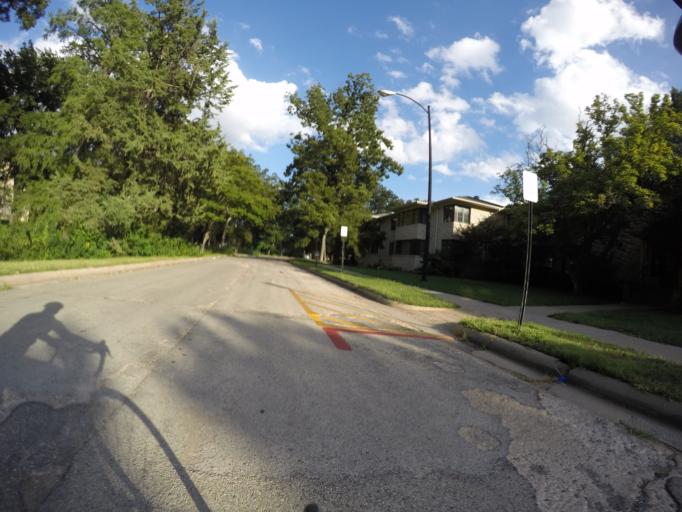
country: US
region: Kansas
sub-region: Riley County
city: Manhattan
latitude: 39.1916
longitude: -96.5782
